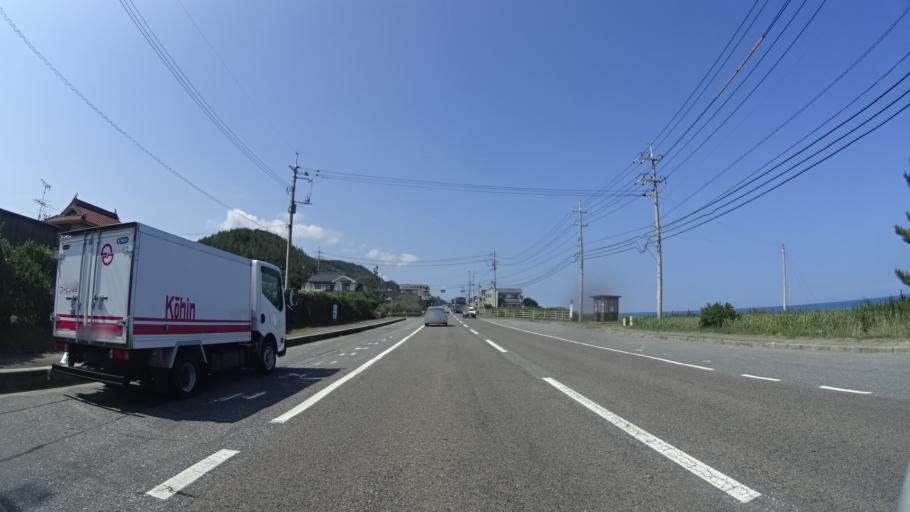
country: JP
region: Shimane
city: Masuda
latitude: 34.6870
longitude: 131.7958
